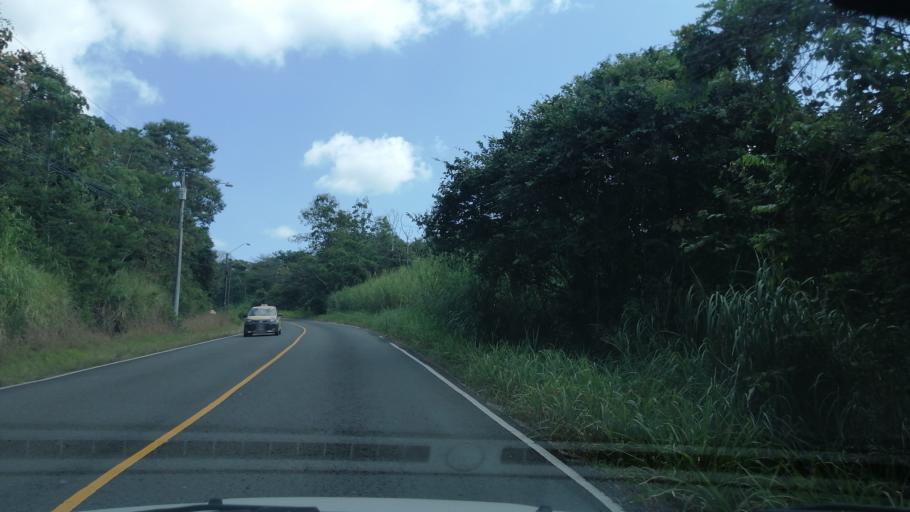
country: PA
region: Panama
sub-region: Distrito de Panama
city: Ancon
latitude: 8.9054
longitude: -79.5699
